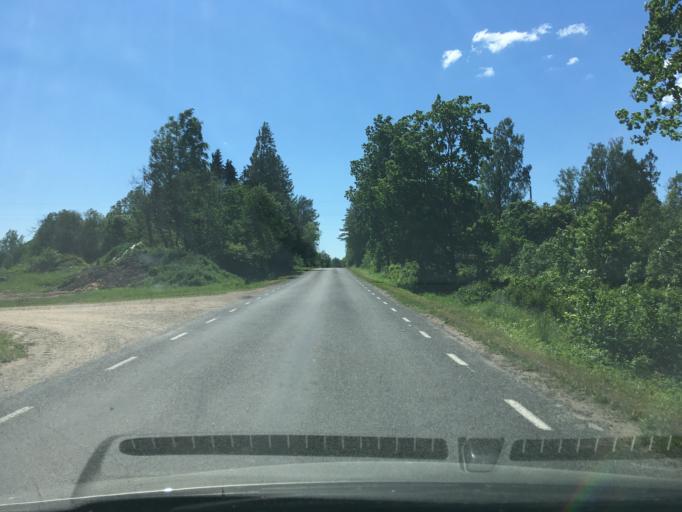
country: EE
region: Raplamaa
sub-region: Kohila vald
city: Kohila
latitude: 59.1311
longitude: 24.8415
